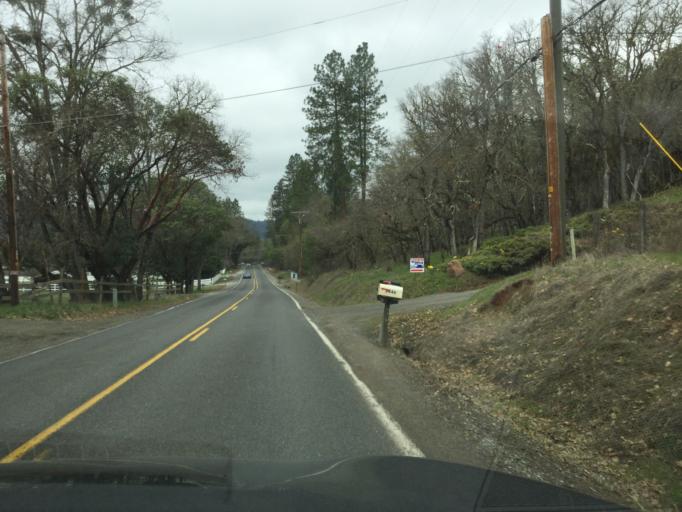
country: US
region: Oregon
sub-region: Jackson County
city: Gold Hill
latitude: 42.3959
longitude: -123.0030
